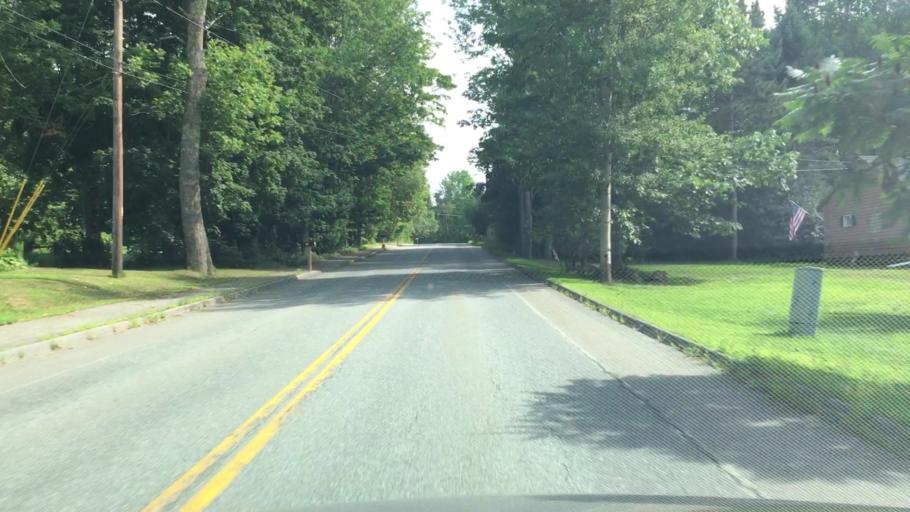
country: US
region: Maine
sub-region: Penobscot County
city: Hampden
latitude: 44.7336
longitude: -68.8592
